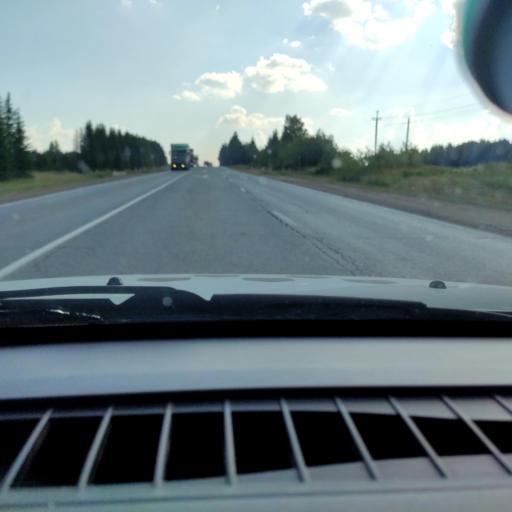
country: RU
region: Perm
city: Nytva
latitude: 57.9636
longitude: 55.1684
